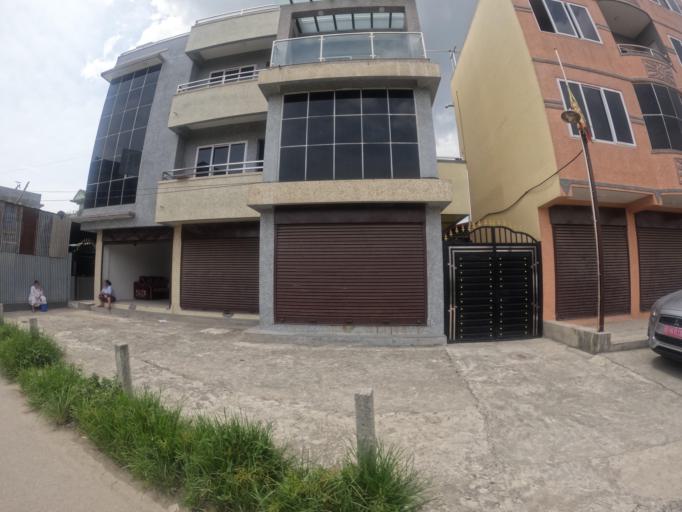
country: NP
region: Central Region
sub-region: Bagmati Zone
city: Bhaktapur
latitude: 27.6891
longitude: 85.3862
